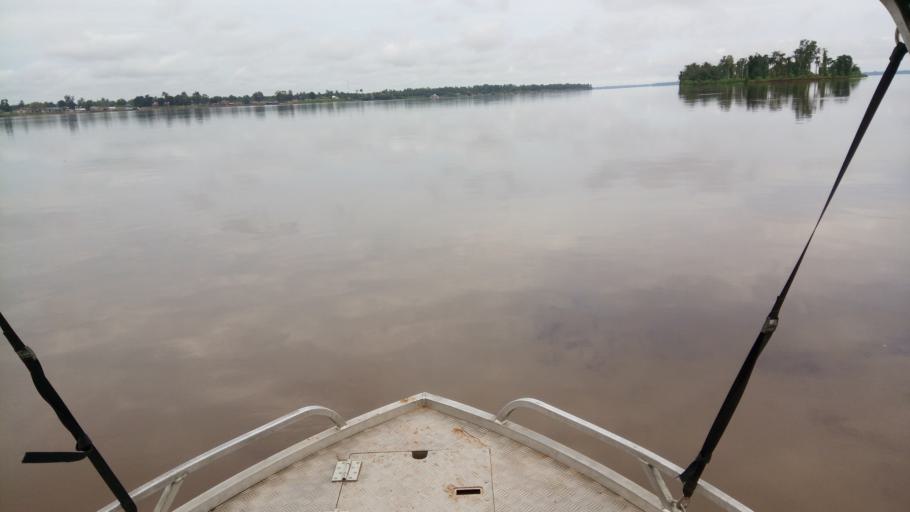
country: CD
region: Eastern Province
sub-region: Sous-Region de la Tshopo
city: Yangambi
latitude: 0.7761
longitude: 24.2843
